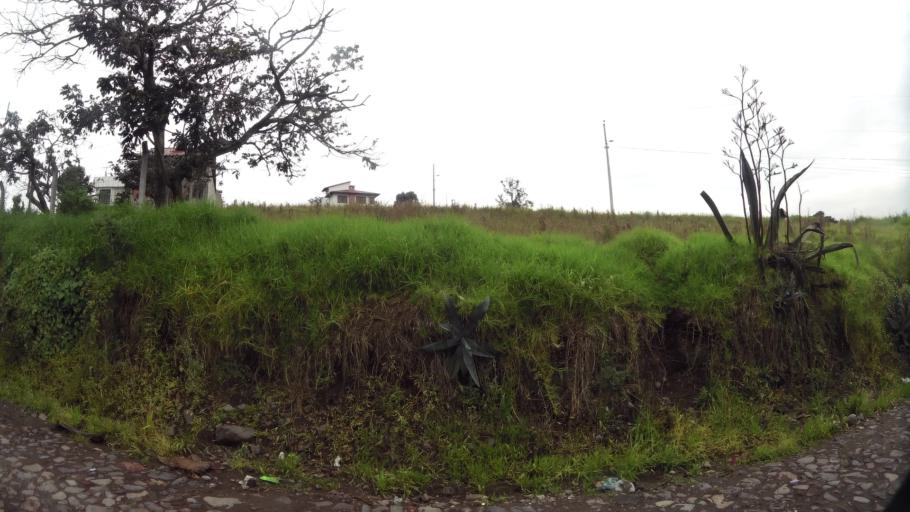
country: EC
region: Pichincha
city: Sangolqui
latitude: -0.2963
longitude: -78.4363
